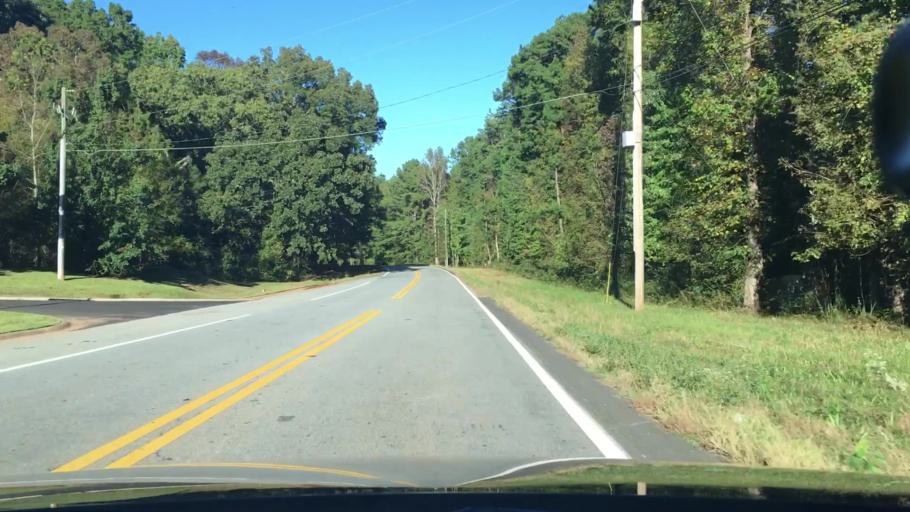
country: US
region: Georgia
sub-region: Coweta County
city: East Newnan
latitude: 33.4120
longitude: -84.7053
